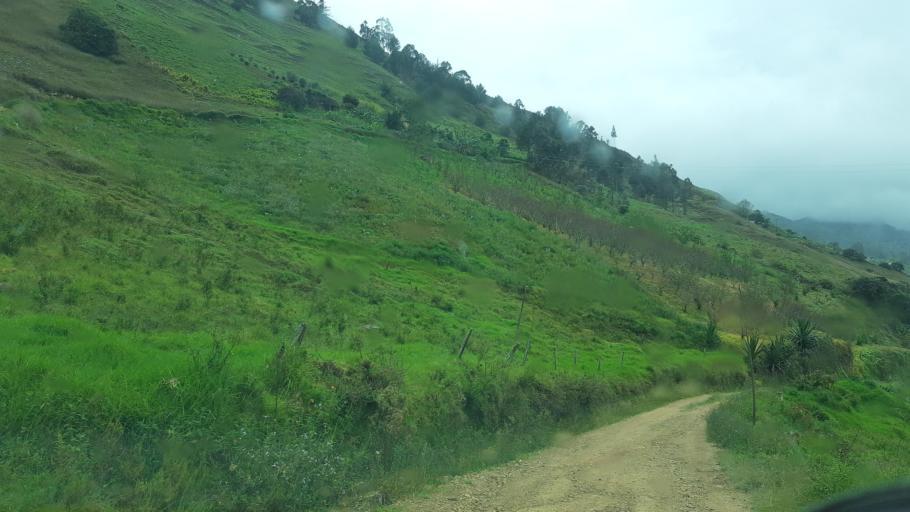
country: CO
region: Boyaca
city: Tibana
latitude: 5.3028
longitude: -73.4349
